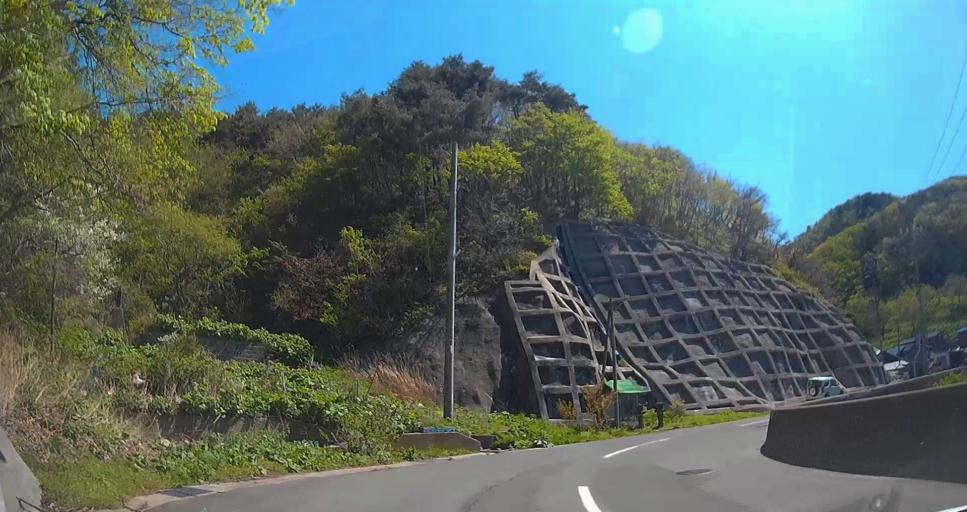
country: JP
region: Aomori
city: Aomori Shi
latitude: 41.1387
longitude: 140.7790
